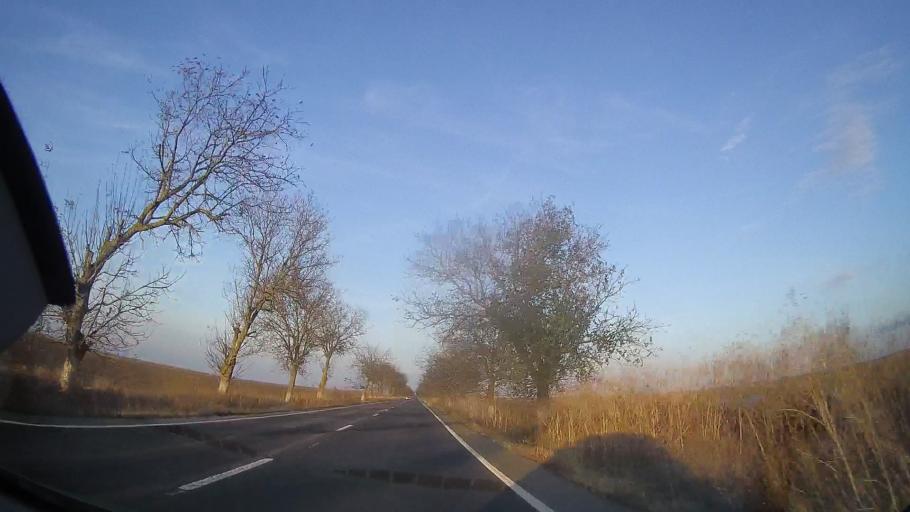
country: RO
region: Constanta
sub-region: Comuna Comana
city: Comana
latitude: 43.9142
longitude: 28.3410
